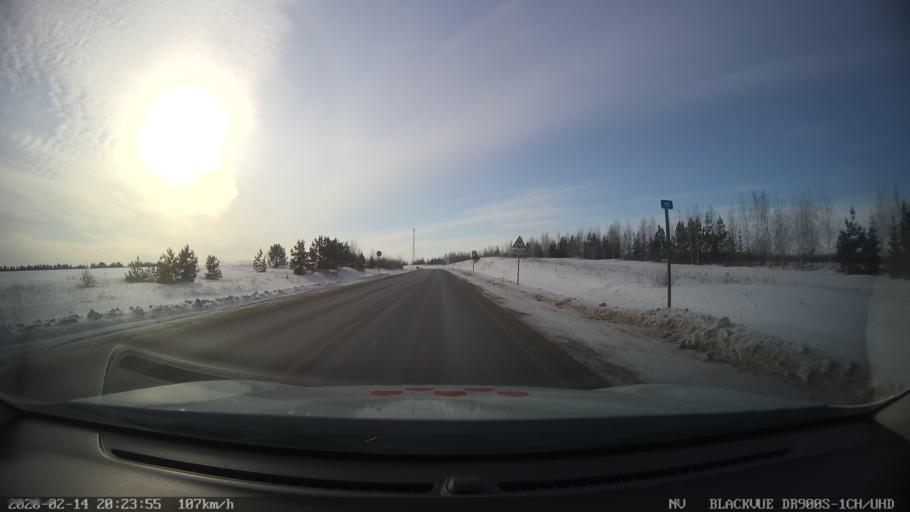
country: RU
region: Tatarstan
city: Verkhniy Uslon
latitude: 55.5207
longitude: 48.9678
